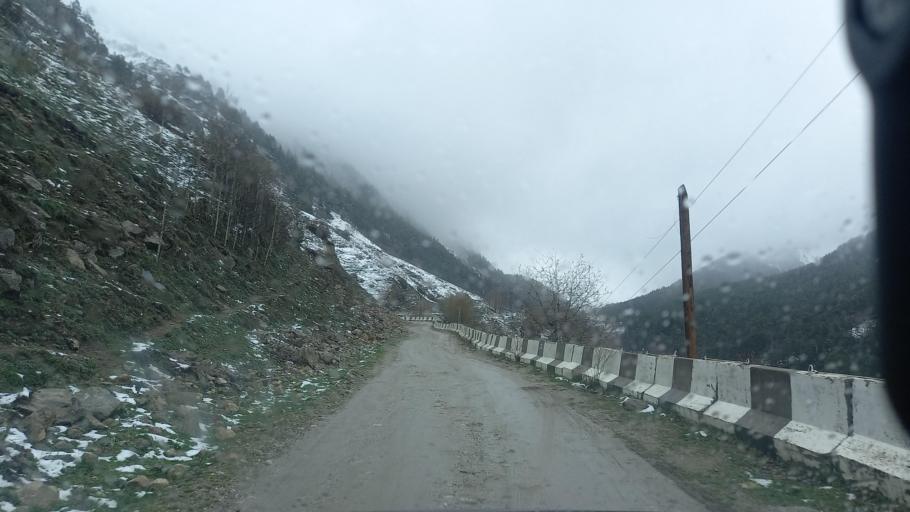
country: RU
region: Kabardino-Balkariya
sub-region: El'brusskiy Rayon
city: El'brus
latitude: 43.2256
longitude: 42.6717
